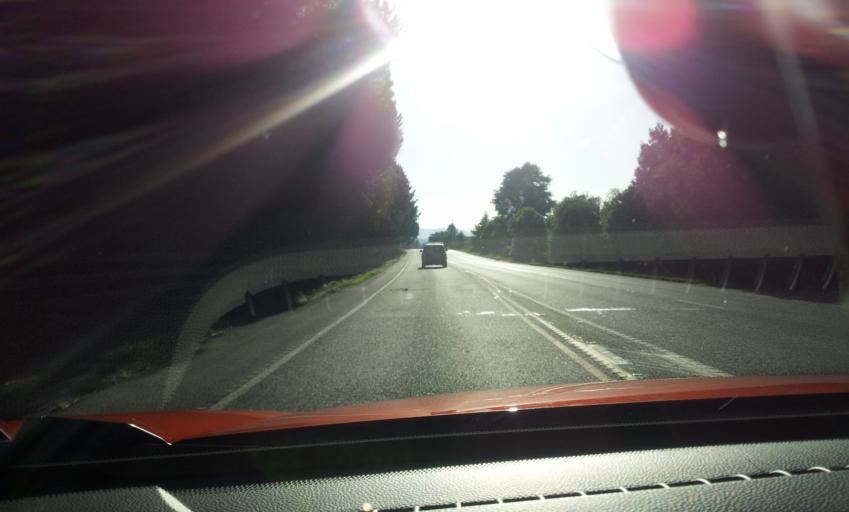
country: NZ
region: Auckland
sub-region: Auckland
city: Pukekohe East
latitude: -37.2253
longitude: 175.0369
